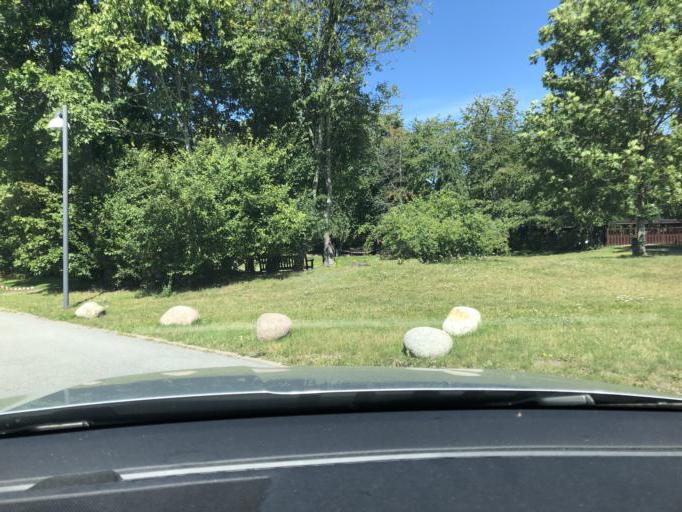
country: SE
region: Stockholm
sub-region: Botkyrka Kommun
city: Tullinge
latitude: 59.2200
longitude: 17.9327
